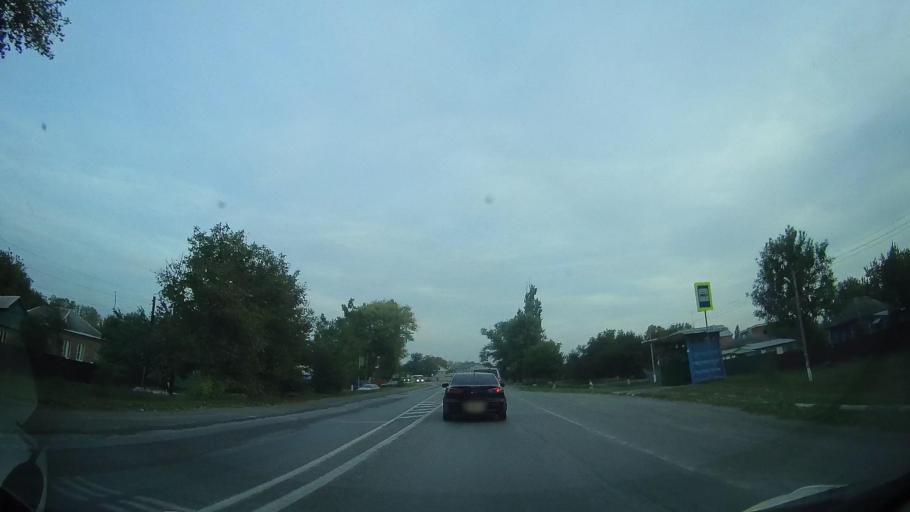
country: RU
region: Rostov
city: Kirovskaya
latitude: 46.9829
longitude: 40.0340
